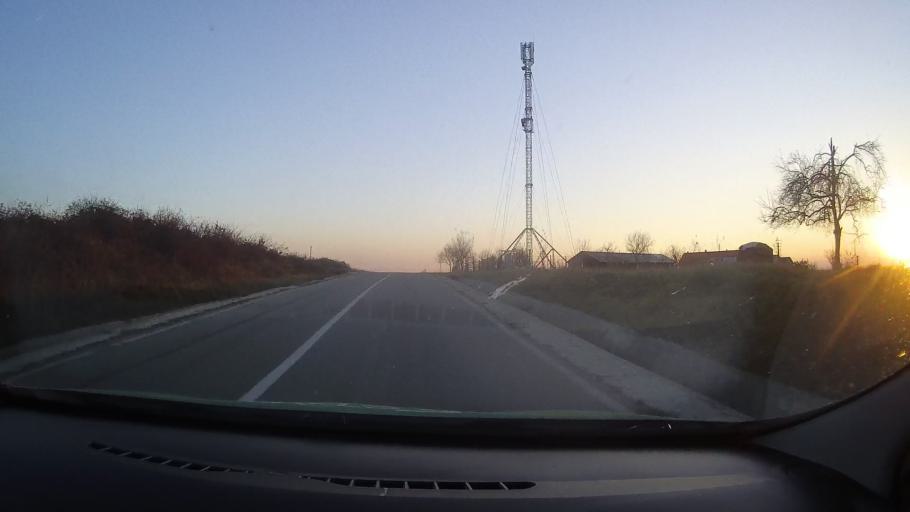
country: RO
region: Timis
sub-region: Comuna Manastiur
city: Manastiur
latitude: 45.8242
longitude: 22.0715
